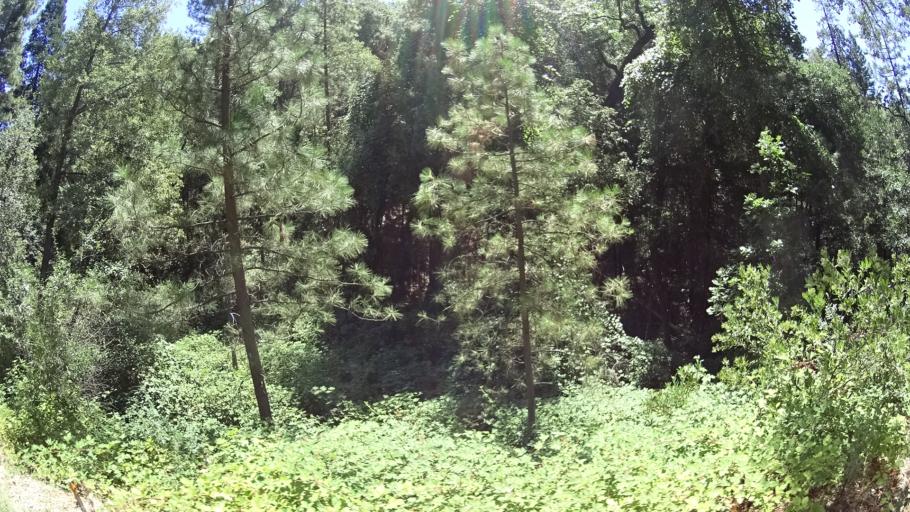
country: US
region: California
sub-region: Calaveras County
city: Forest Meadows
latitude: 38.1493
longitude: -120.4064
